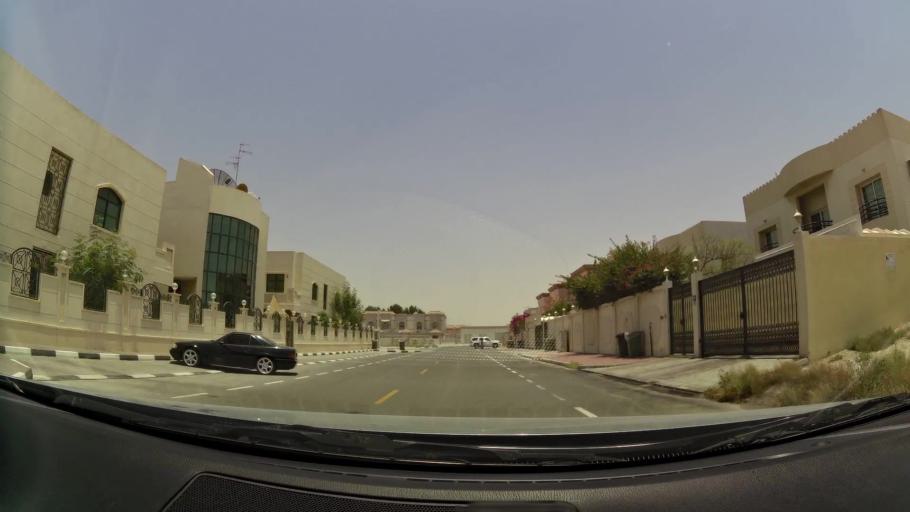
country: AE
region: Dubai
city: Dubai
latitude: 25.1746
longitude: 55.2377
